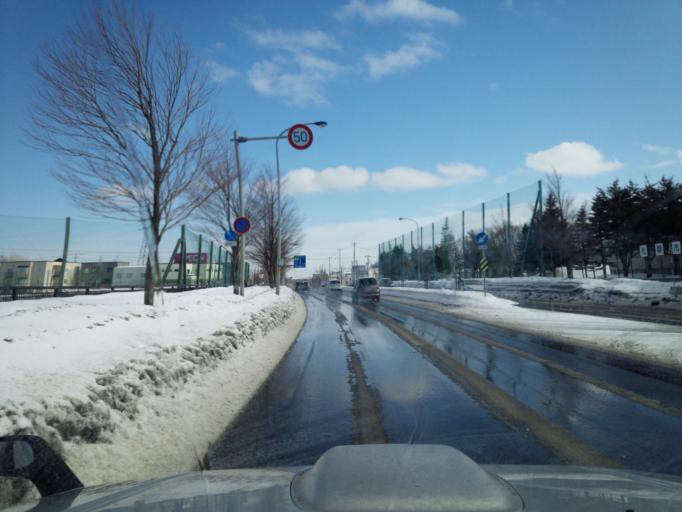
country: JP
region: Hokkaido
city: Kitahiroshima
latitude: 42.9931
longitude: 141.4559
